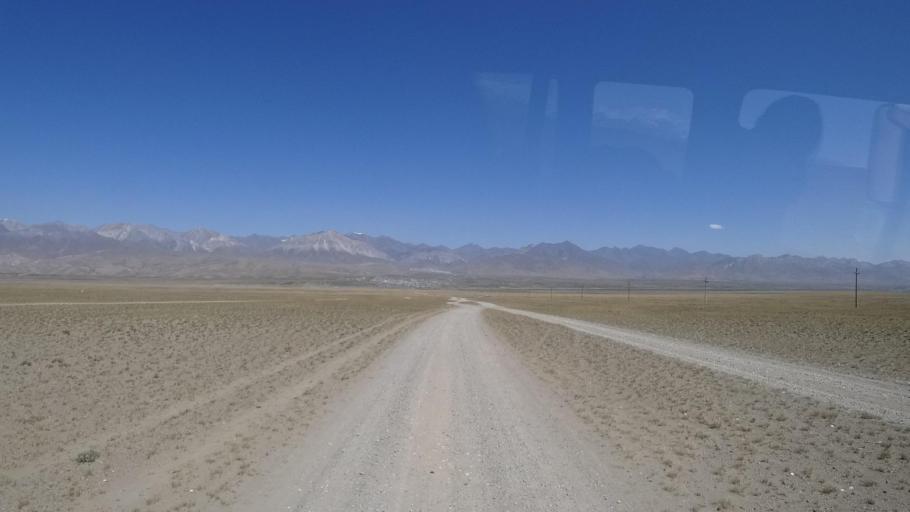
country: KG
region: Osh
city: Gul'cha
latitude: 39.6156
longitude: 72.8747
